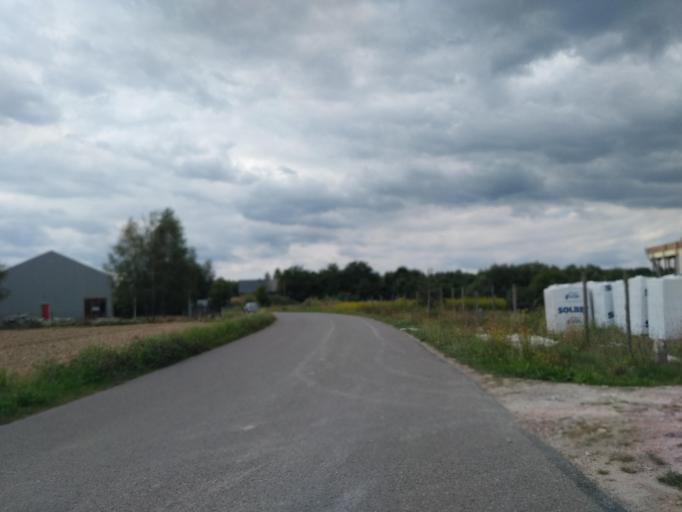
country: PL
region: Subcarpathian Voivodeship
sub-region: Powiat rzeszowski
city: Tyczyn
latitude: 49.9340
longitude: 22.0571
